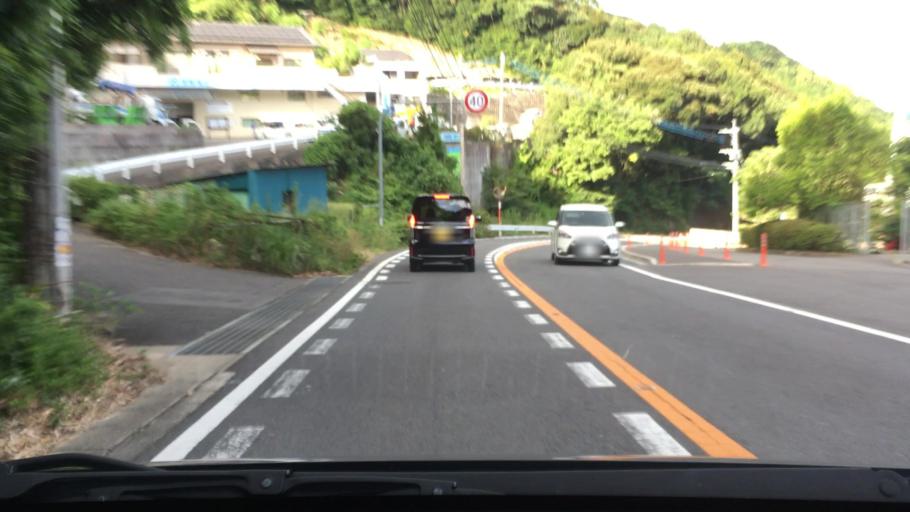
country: JP
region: Nagasaki
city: Togitsu
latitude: 32.8096
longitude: 129.8157
